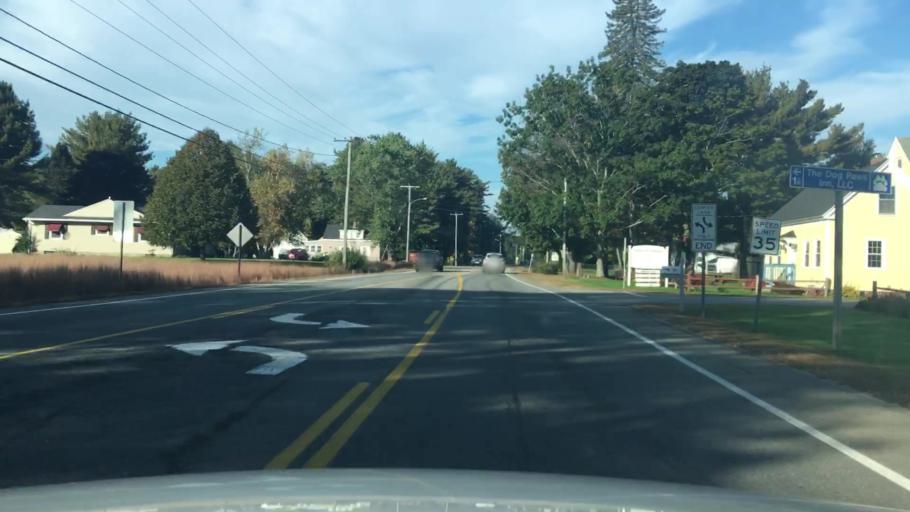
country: US
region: Maine
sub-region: Cumberland County
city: Westbrook
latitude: 43.6420
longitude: -70.3995
